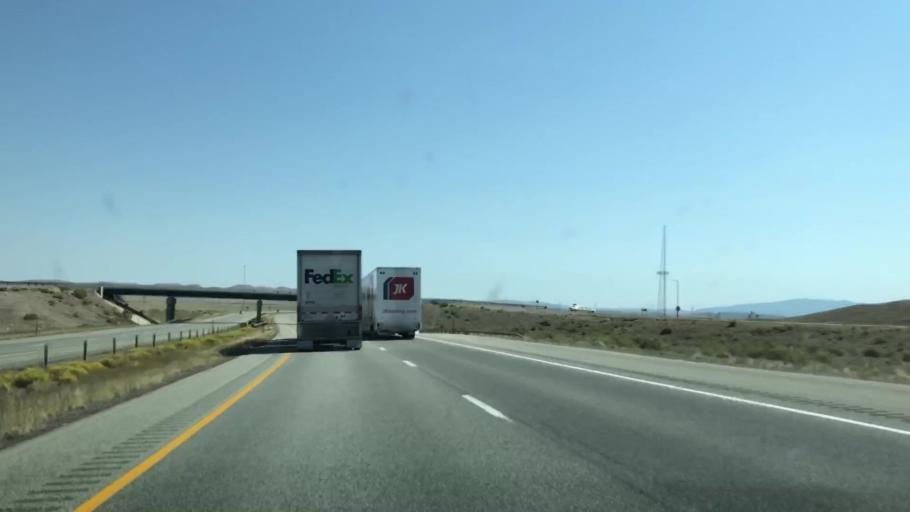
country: US
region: Wyoming
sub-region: Carbon County
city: Rawlins
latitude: 41.7717
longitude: -107.0844
